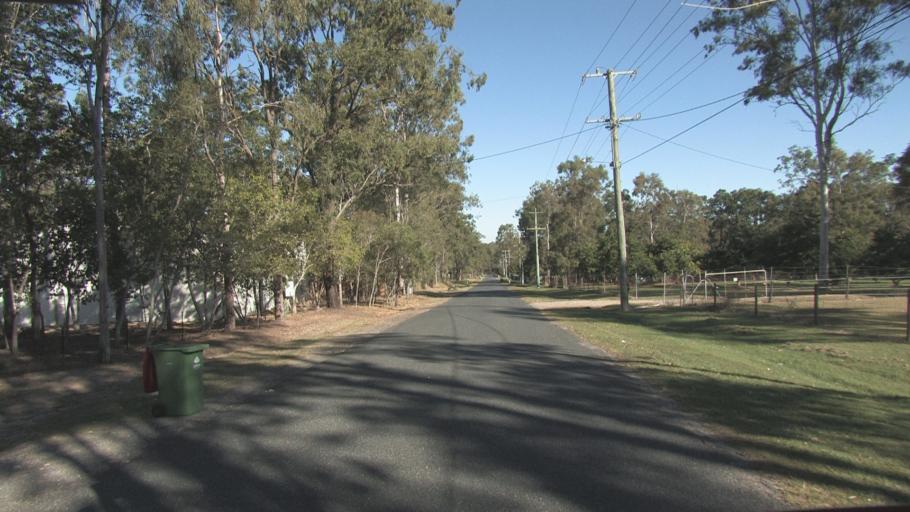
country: AU
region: Queensland
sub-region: Logan
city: Park Ridge South
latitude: -27.7281
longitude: 153.0119
